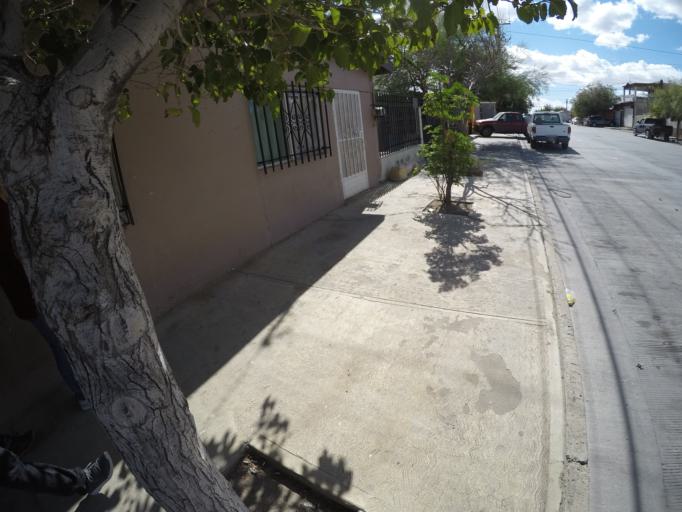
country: MX
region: Chihuahua
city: Ciudad Juarez
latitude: 31.6910
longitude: -106.4817
